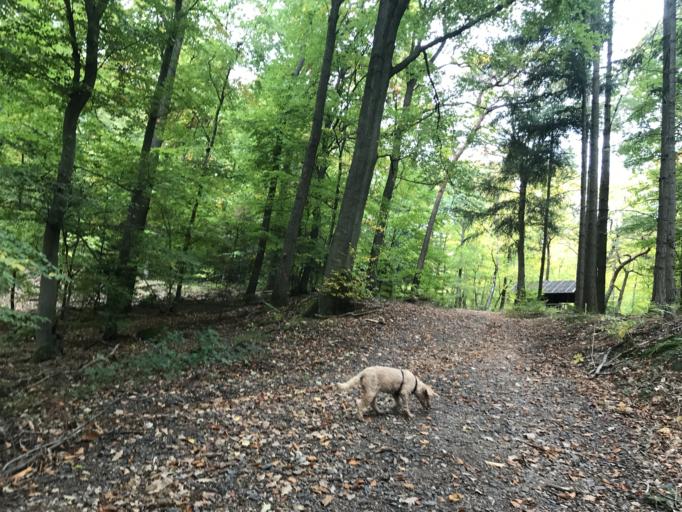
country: DE
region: Rheinland-Pfalz
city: Kirchheimbolanden
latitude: 49.6563
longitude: 7.9909
